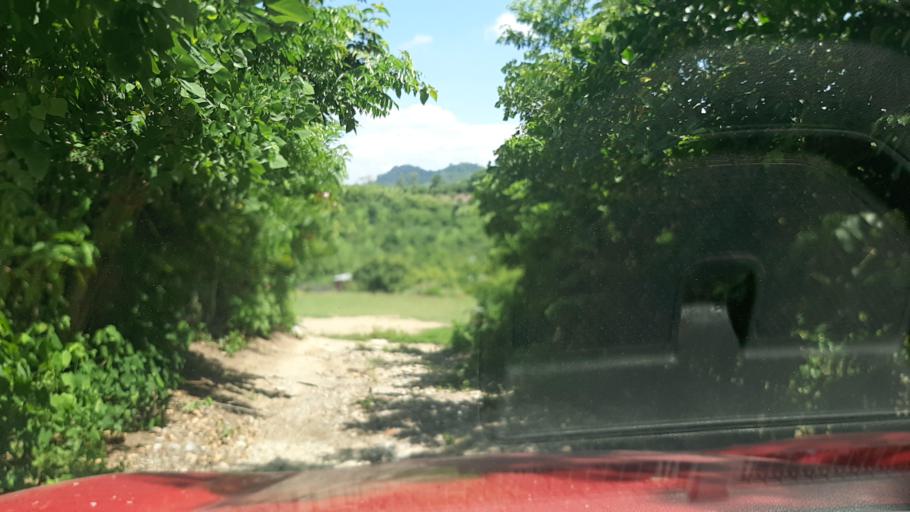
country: MX
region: Veracruz
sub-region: Poza Rica de Hidalgo
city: El Mollejon
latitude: 20.5444
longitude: -97.4078
